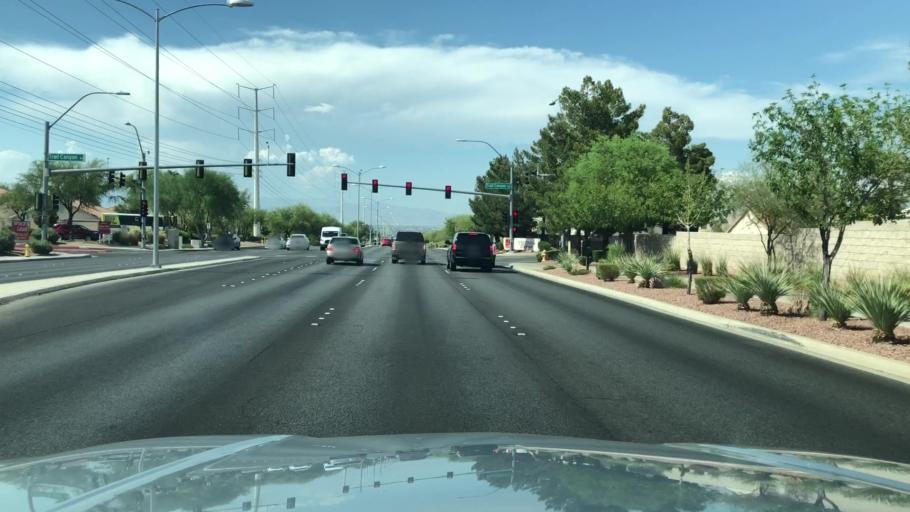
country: US
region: Nevada
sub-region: Clark County
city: Whitney
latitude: 36.0444
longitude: -115.0466
